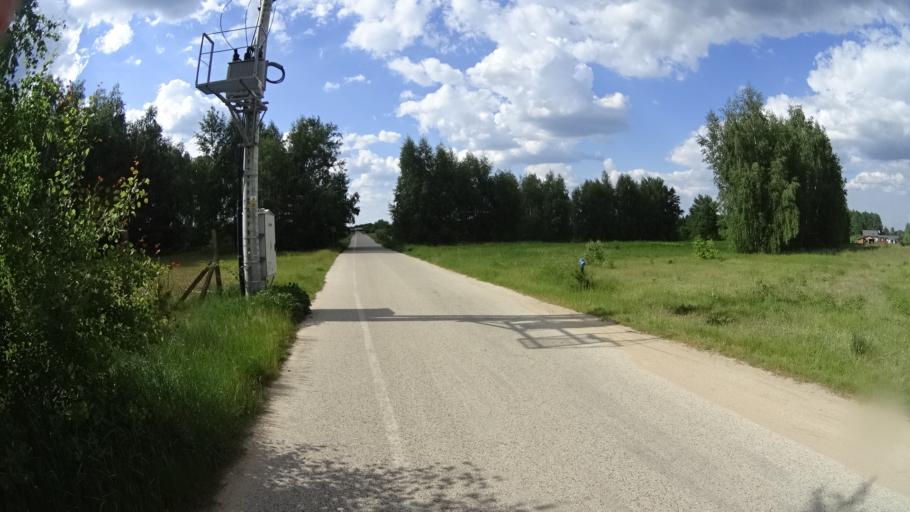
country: PL
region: Masovian Voivodeship
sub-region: Powiat piaseczynski
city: Tarczyn
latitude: 52.0012
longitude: 20.8332
